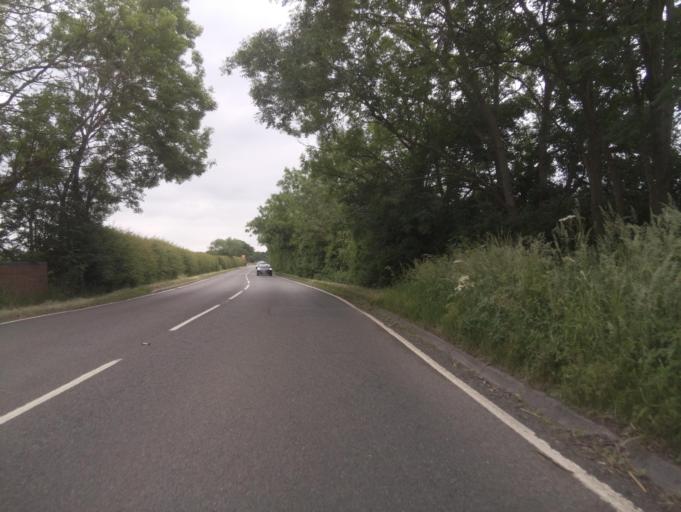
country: GB
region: England
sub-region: Leicestershire
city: Melton Mowbray
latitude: 52.7368
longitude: -0.8554
